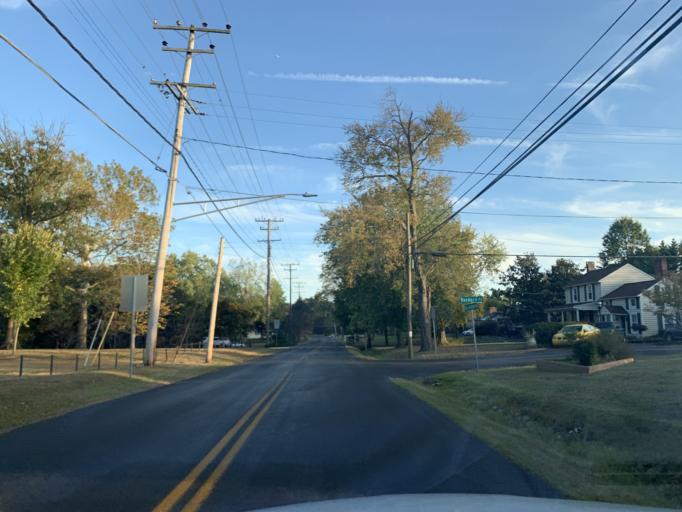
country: US
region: Maryland
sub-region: Harford County
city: Fallston
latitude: 39.5091
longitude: -76.4068
